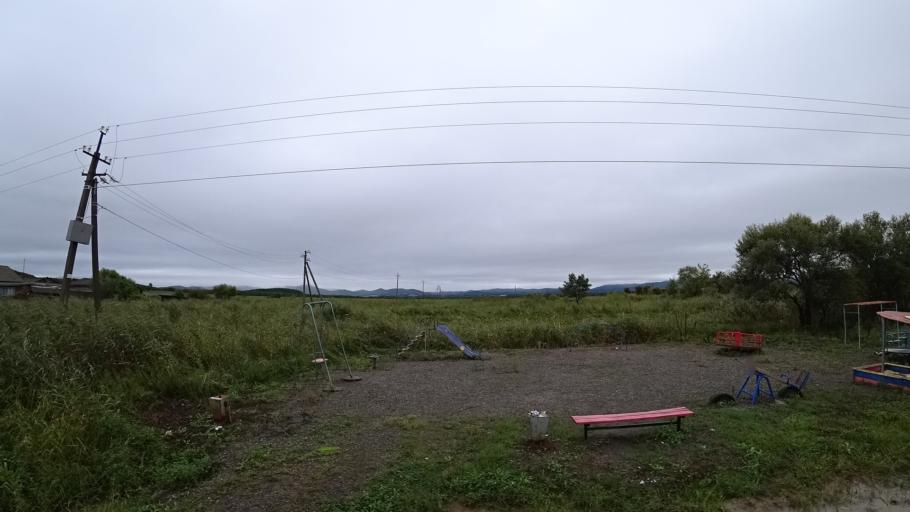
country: RU
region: Primorskiy
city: Monastyrishche
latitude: 44.2314
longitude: 132.4592
